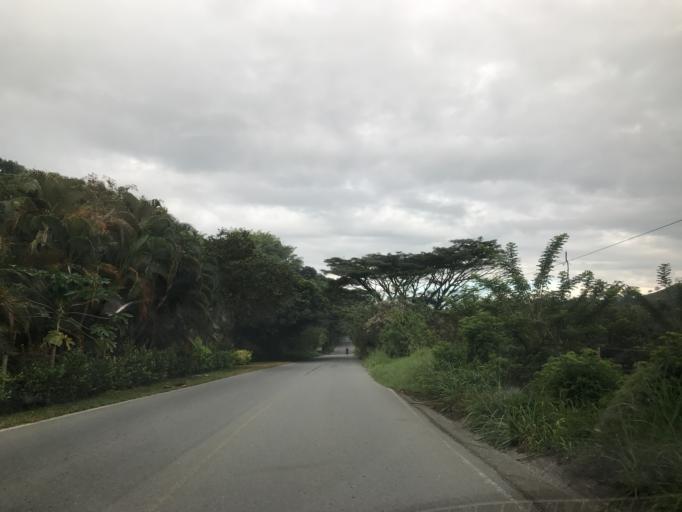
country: CO
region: Quindio
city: Cordoba
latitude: 4.4037
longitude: -75.7343
